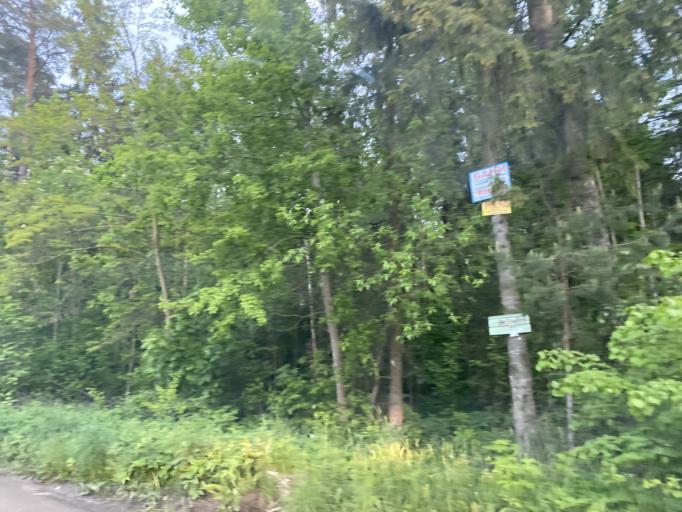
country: BY
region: Minsk
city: Rudzyensk
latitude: 53.6087
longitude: 27.7850
